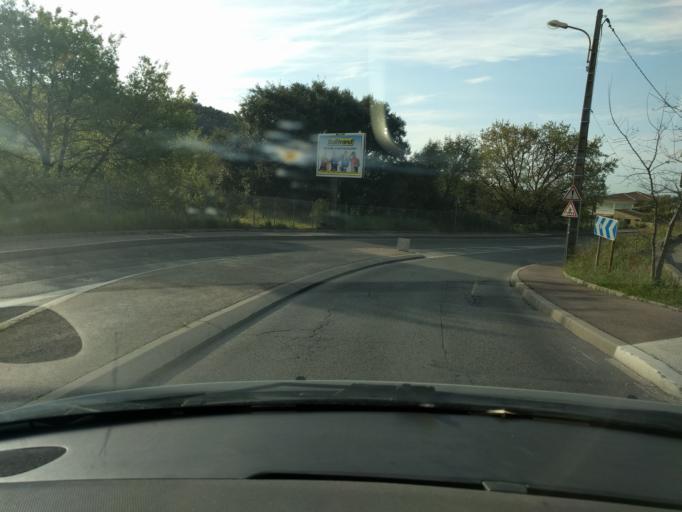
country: FR
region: Provence-Alpes-Cote d'Azur
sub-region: Departement des Alpes-Maritimes
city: Cannes
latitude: 43.5630
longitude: 6.9774
